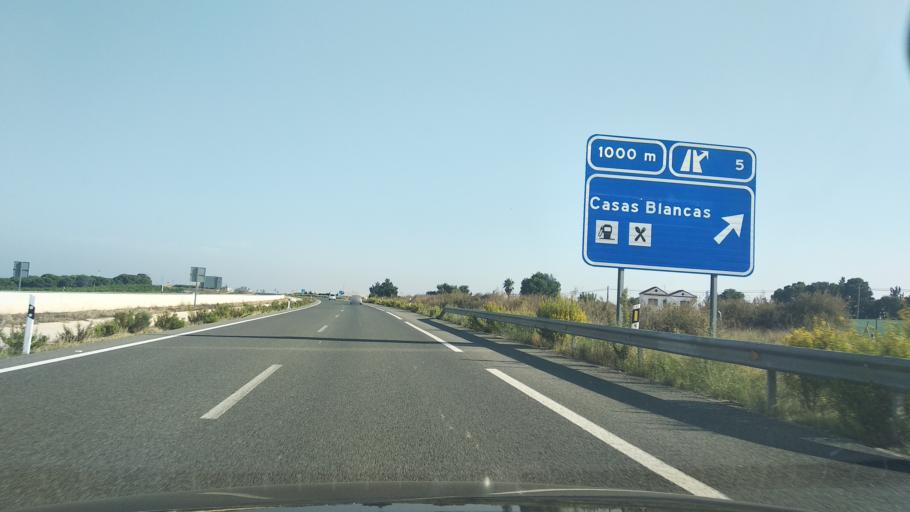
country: ES
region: Murcia
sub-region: Murcia
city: San Javier
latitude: 37.8583
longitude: -0.8886
